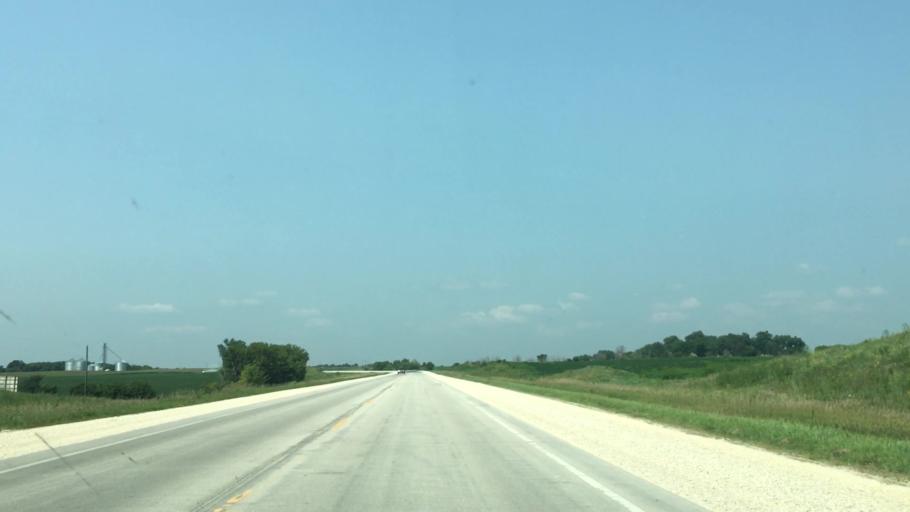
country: US
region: Iowa
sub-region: Winneshiek County
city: Decorah
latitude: 43.3586
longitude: -91.8044
